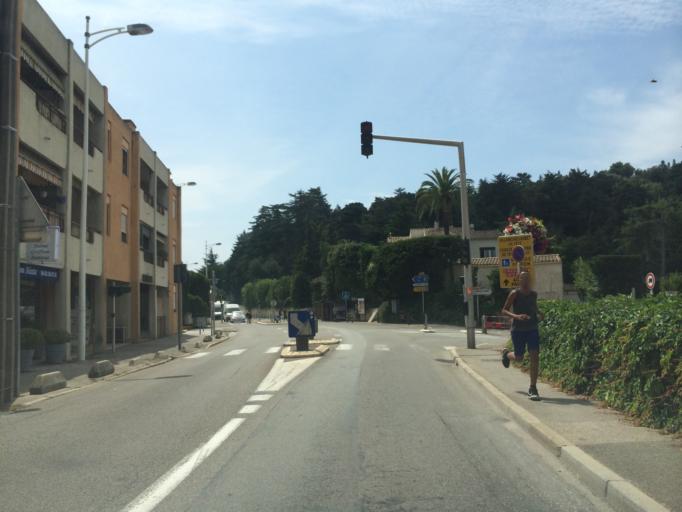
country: FR
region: Provence-Alpes-Cote d'Azur
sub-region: Departement des Alpes-Maritimes
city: Villeneuve-Loubet
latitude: 43.6636
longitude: 7.1249
